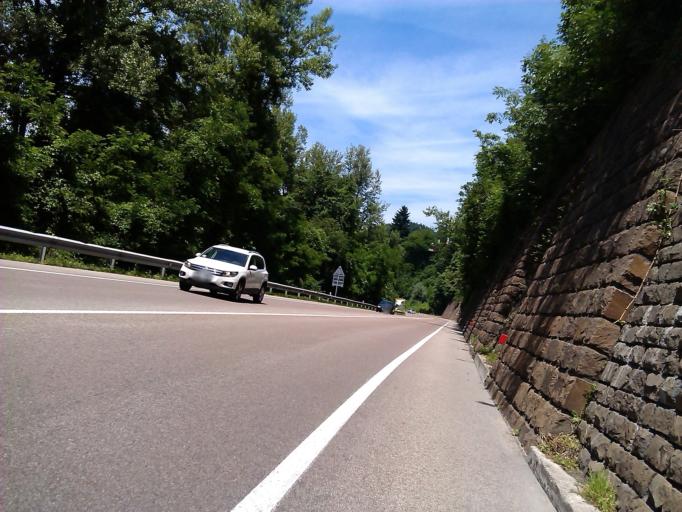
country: IT
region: Trentino-Alto Adige
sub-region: Provincia di Trento
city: Tenna
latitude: 46.0313
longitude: 11.2452
